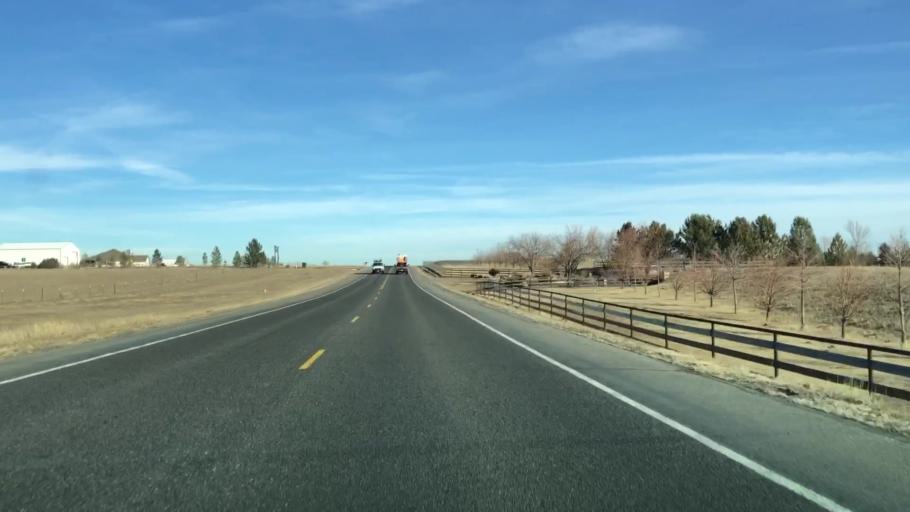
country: US
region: Colorado
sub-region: Weld County
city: Windsor
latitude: 40.4276
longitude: -104.9443
